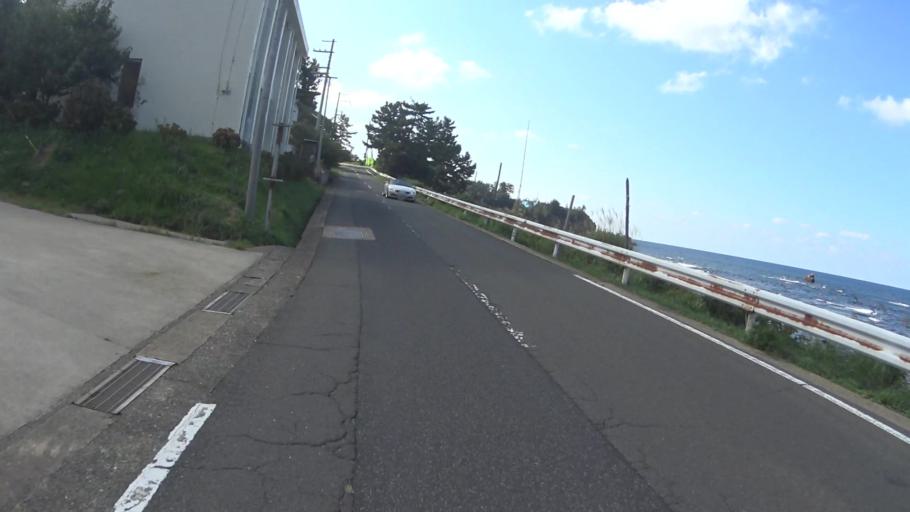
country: JP
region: Kyoto
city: Miyazu
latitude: 35.7642
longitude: 135.2018
